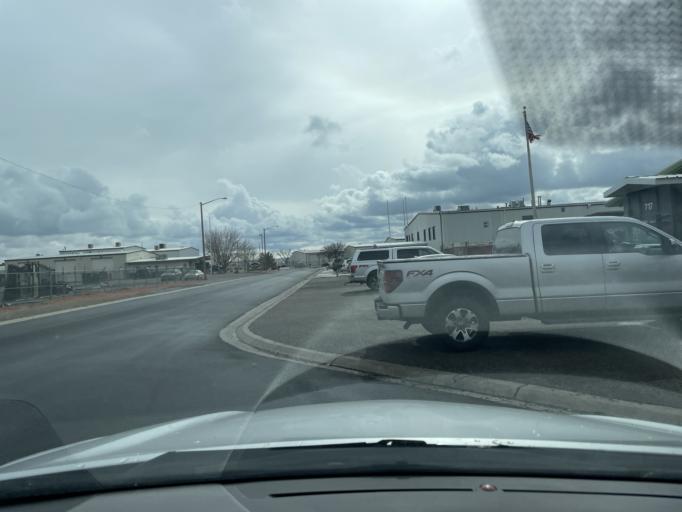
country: US
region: Colorado
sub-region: Mesa County
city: Redlands
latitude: 39.1091
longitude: -108.6330
